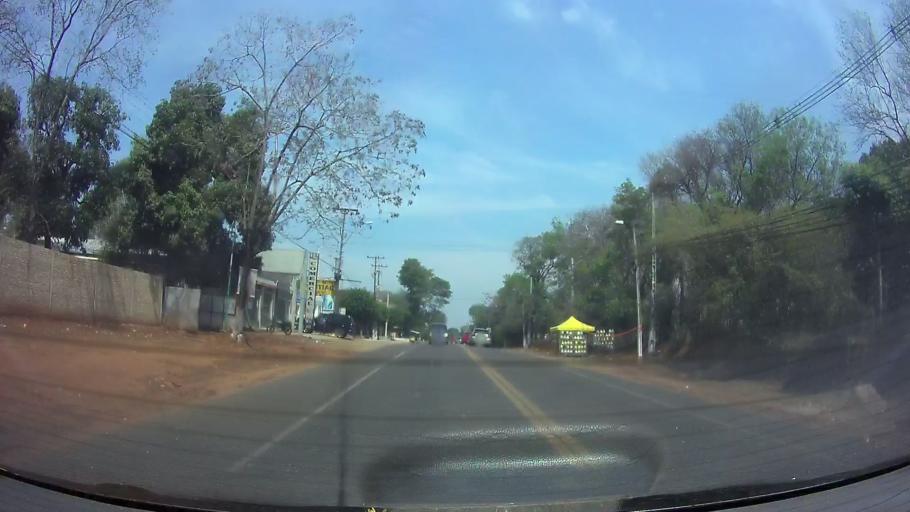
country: PY
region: Central
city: Capiata
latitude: -25.3803
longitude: -57.4745
